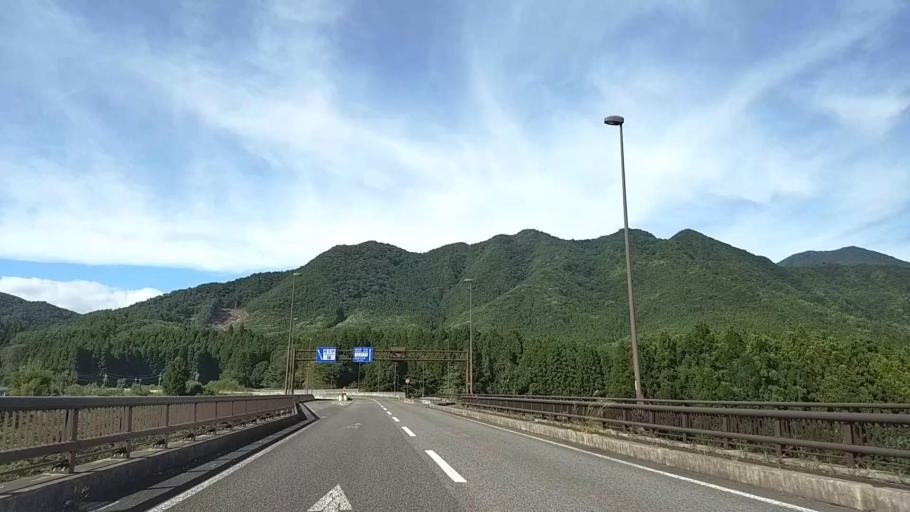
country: JP
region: Tochigi
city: Imaichi
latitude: 36.8563
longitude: 139.7250
